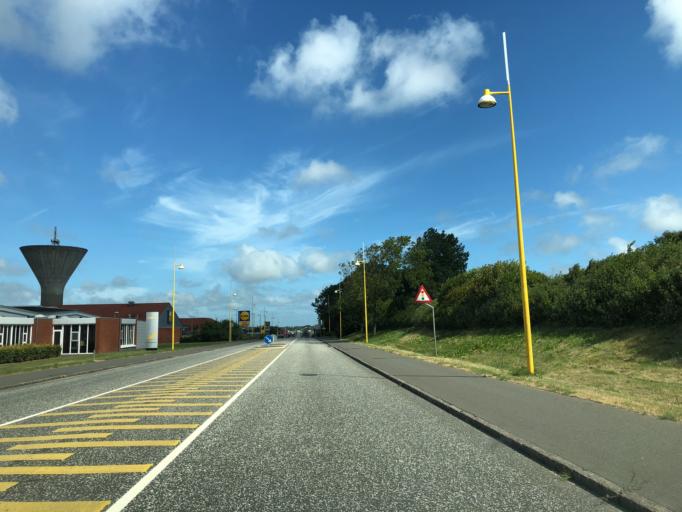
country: DK
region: Central Jutland
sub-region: Struer Kommune
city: Struer
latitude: 56.4853
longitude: 8.5836
